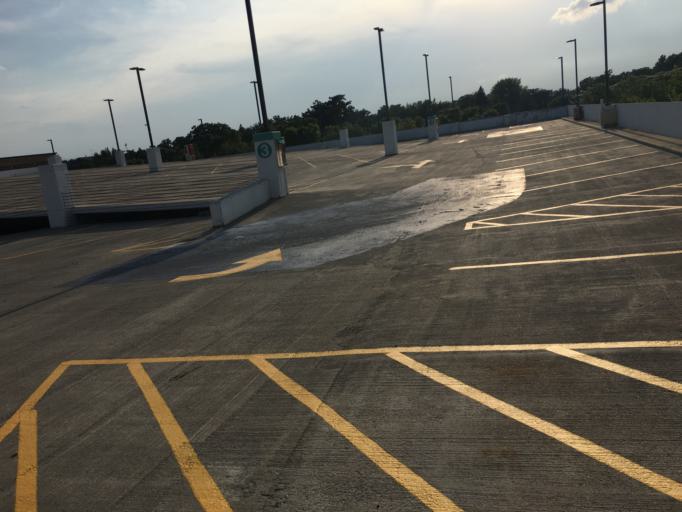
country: US
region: Minnesota
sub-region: Stearns County
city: Saint Cloud
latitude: 45.5547
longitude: -94.1520
